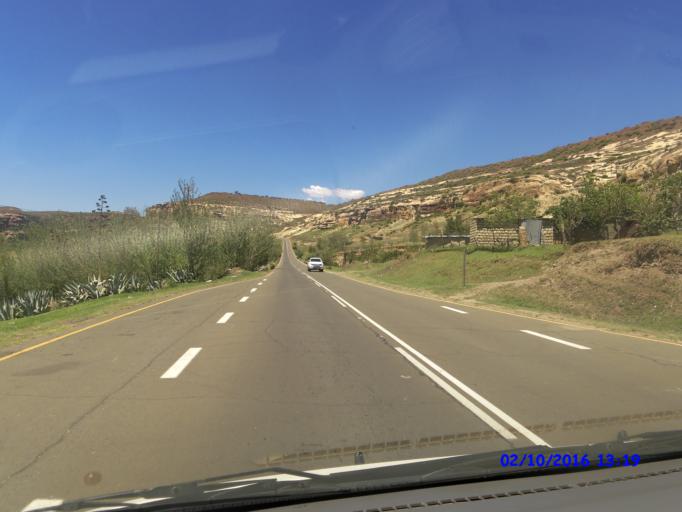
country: LS
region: Maseru
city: Nako
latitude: -29.4237
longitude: 27.6899
